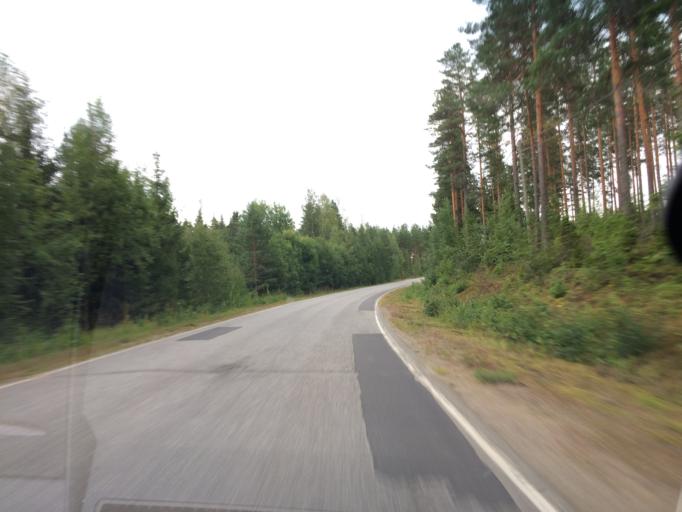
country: FI
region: Haeme
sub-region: Haemeenlinna
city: Tuulos
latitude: 61.2226
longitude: 24.7209
